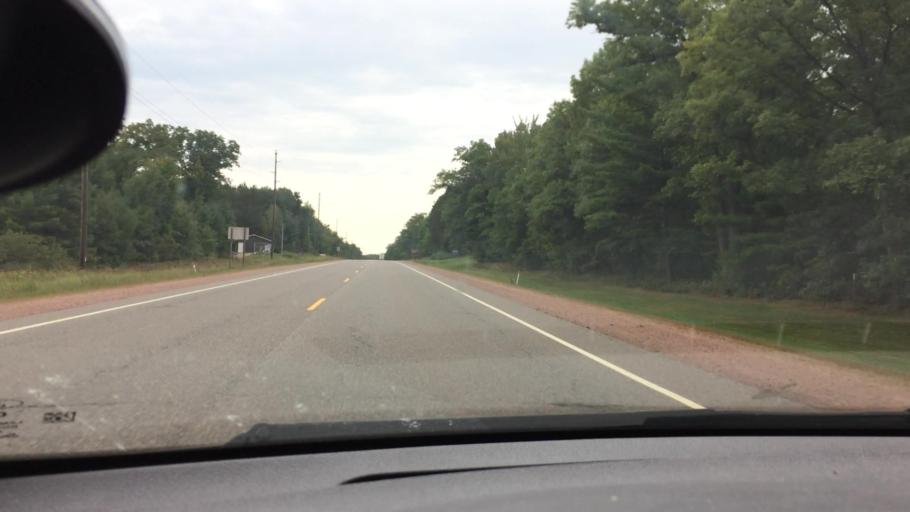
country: US
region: Wisconsin
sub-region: Clark County
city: Neillsville
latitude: 44.5735
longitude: -90.7312
